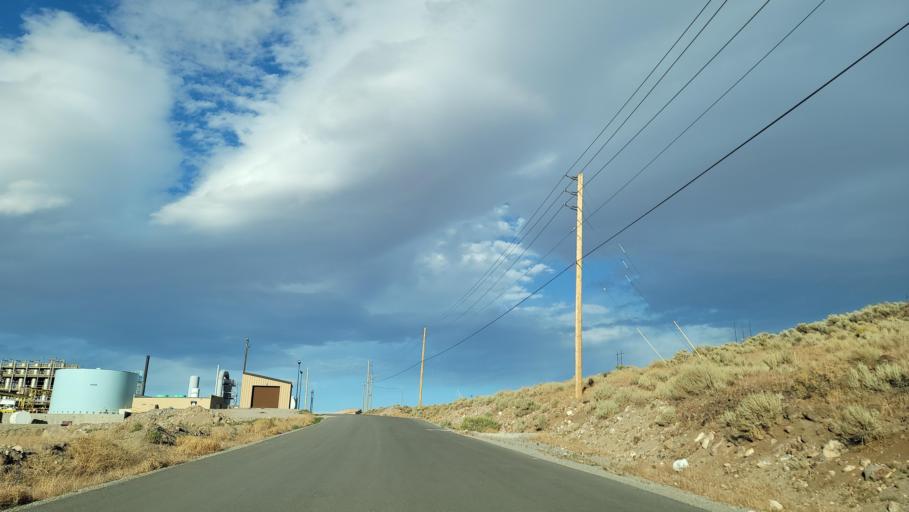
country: US
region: Nevada
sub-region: Washoe County
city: Spanish Springs
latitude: 39.5526
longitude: -119.5223
